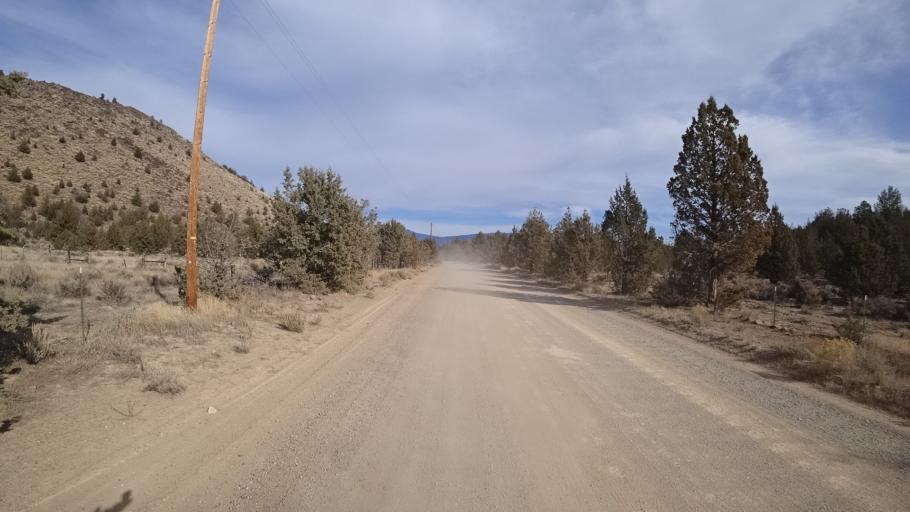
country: US
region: California
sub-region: Siskiyou County
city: Montague
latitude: 41.5817
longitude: -122.4534
